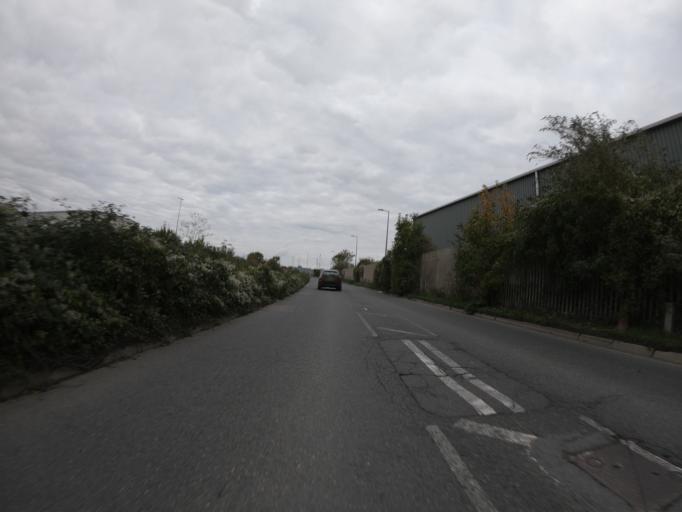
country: GB
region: England
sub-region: Borough of Thurrock
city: Tilbury
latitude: 51.4544
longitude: 0.3638
